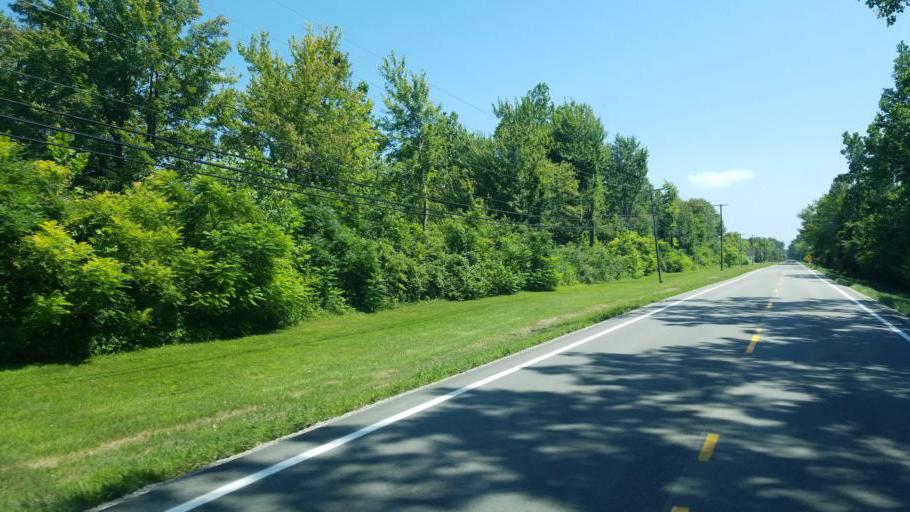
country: US
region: Ohio
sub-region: Erie County
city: Sandusky
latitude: 41.4201
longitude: -82.8177
